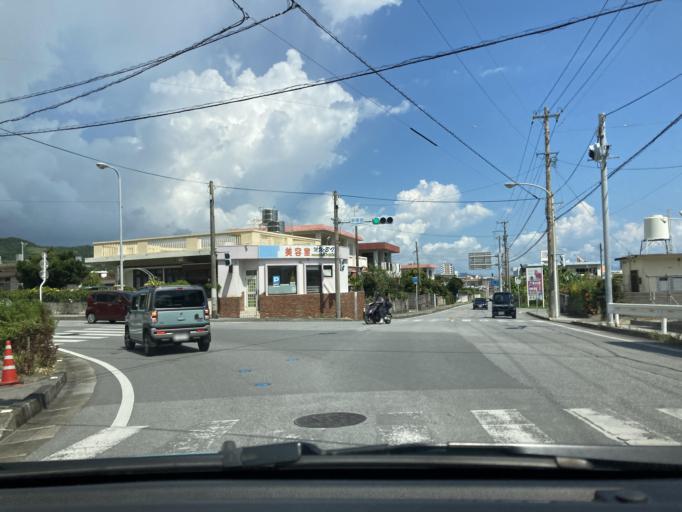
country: JP
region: Okinawa
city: Tomigusuku
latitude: 26.1712
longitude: 127.7725
